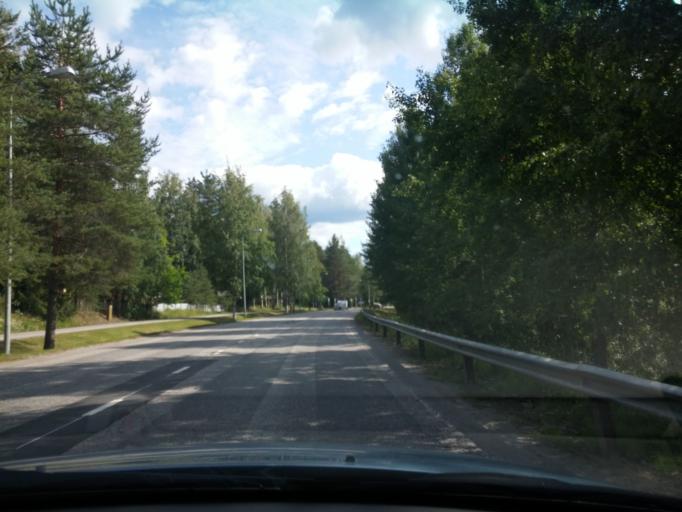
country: FI
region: Central Finland
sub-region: Keuruu
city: Keuruu
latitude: 62.2652
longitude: 24.6987
